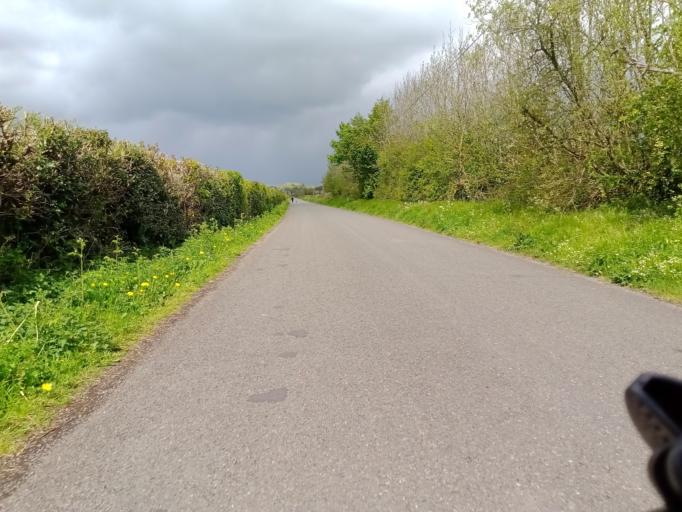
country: IE
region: Leinster
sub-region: Kilkenny
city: Kilkenny
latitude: 52.6759
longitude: -7.2601
